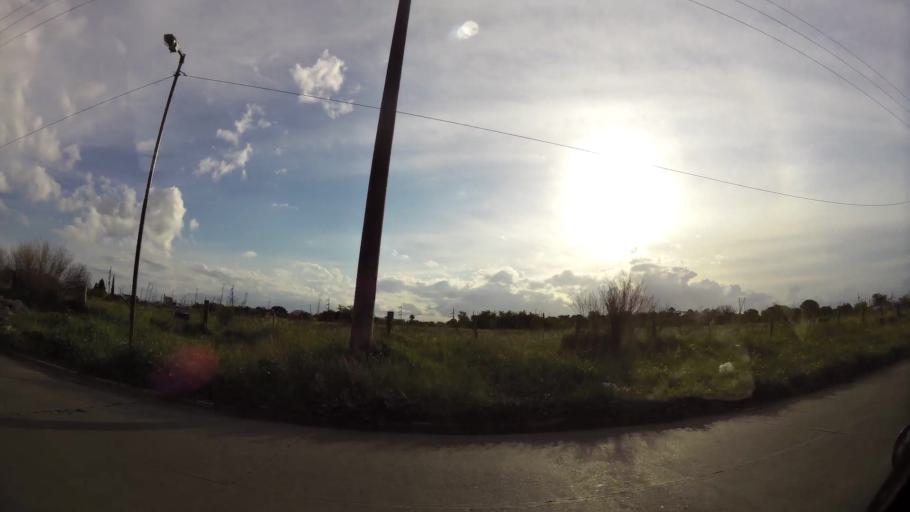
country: AR
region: Buenos Aires
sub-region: Partido de Quilmes
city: Quilmes
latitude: -34.7494
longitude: -58.2628
